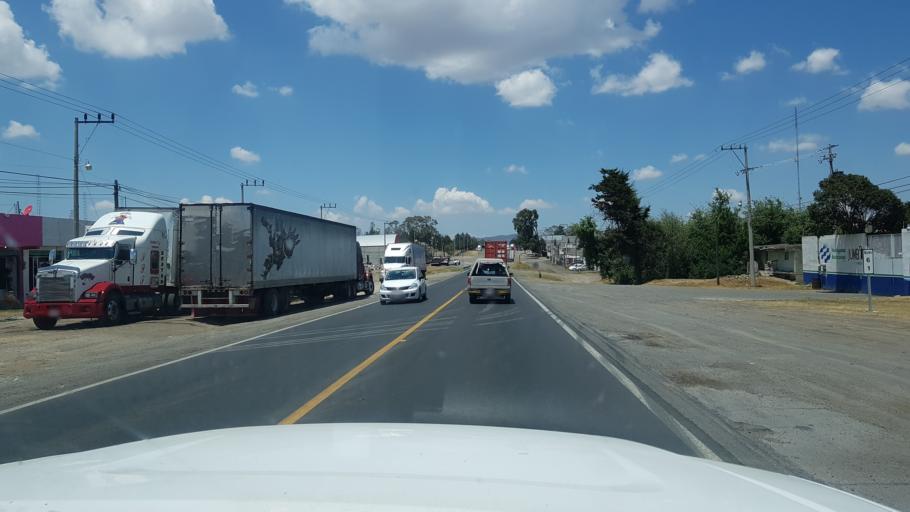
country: MX
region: Hidalgo
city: Calpulalpan
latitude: 19.5877
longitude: -98.5493
